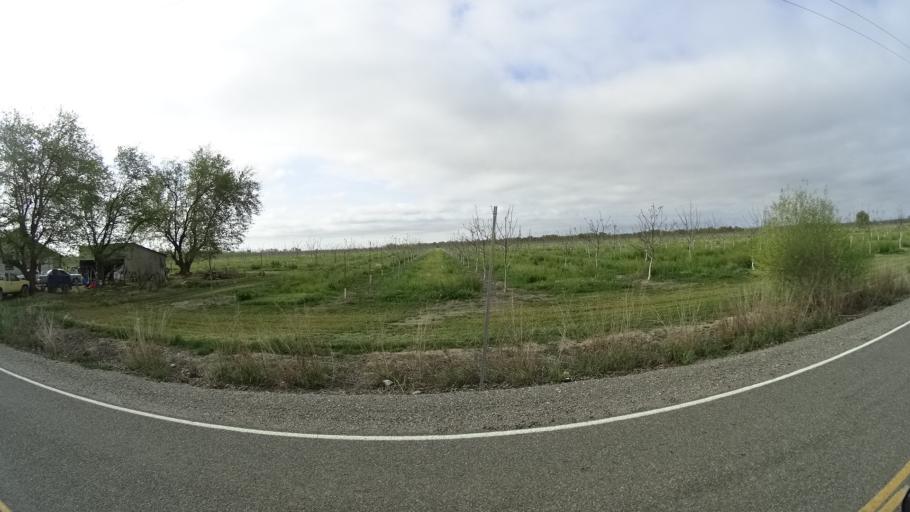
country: US
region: California
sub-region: Colusa County
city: Colusa
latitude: 39.4020
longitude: -121.9685
